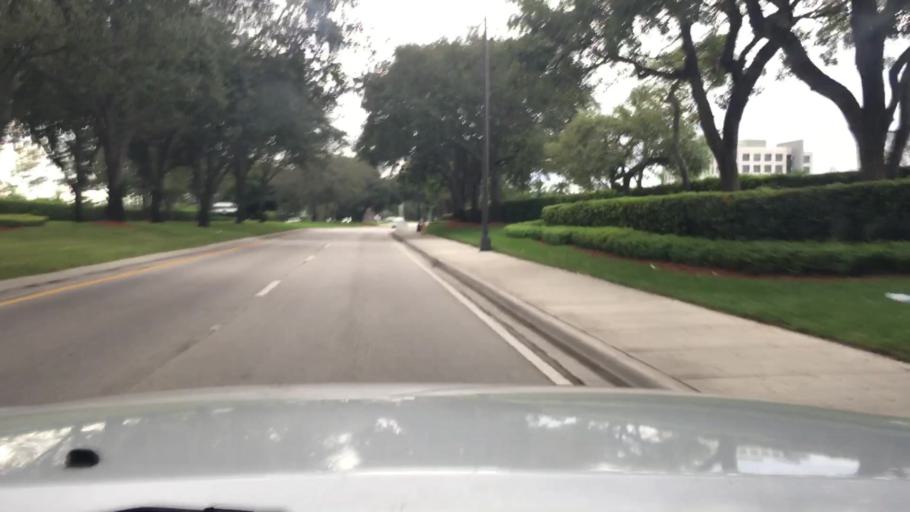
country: US
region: Florida
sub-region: Miami-Dade County
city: West Miami
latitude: 25.7778
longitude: -80.2991
